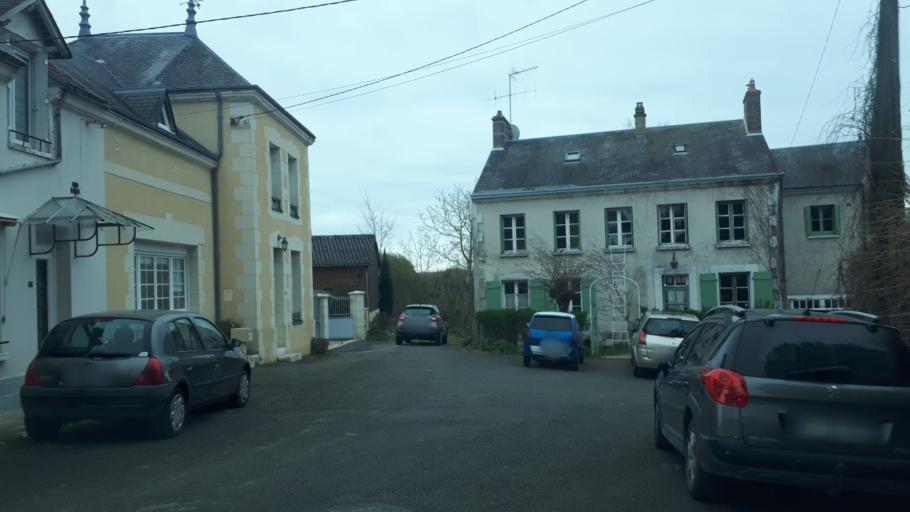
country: FR
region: Centre
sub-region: Departement du Loir-et-Cher
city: Lunay
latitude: 47.7530
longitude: 0.9375
